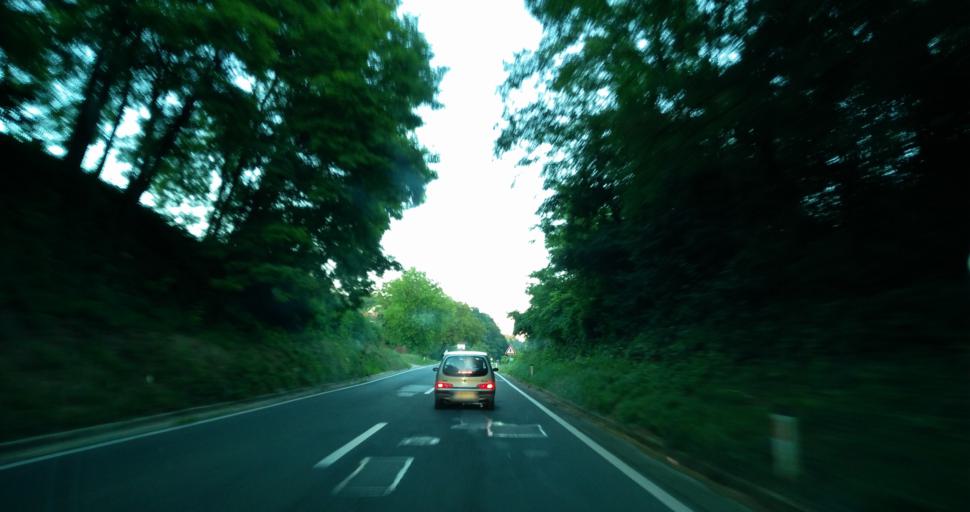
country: BA
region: Republika Srpska
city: Svodna
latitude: 45.0361
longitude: 16.4886
